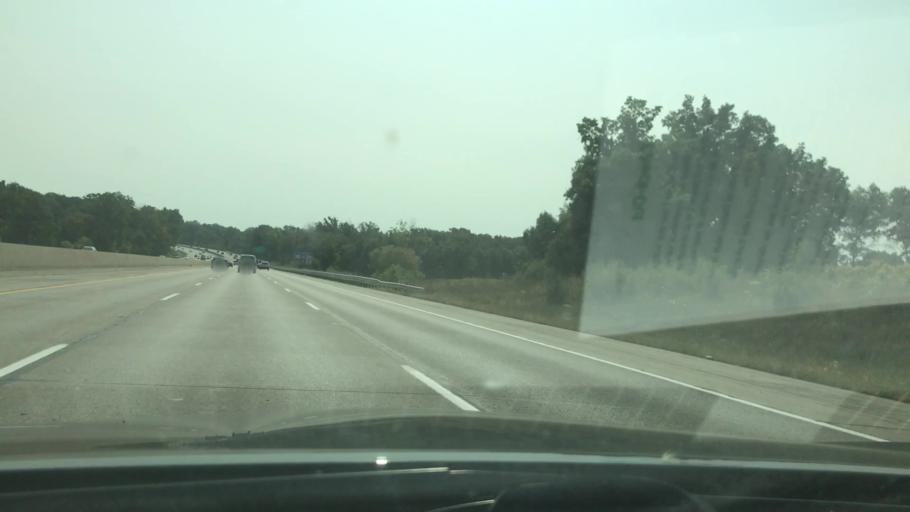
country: US
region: Michigan
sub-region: Livingston County
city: Brighton
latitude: 42.5567
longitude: -83.8215
